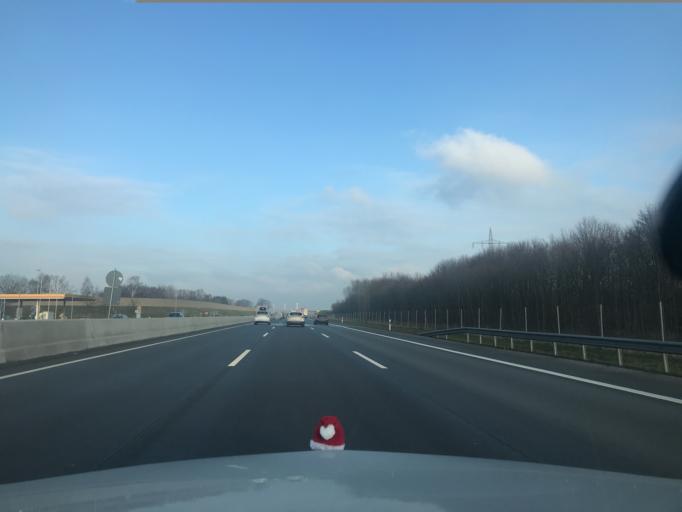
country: DE
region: Schleswig-Holstein
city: Wasbek
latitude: 54.0919
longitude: 9.9309
